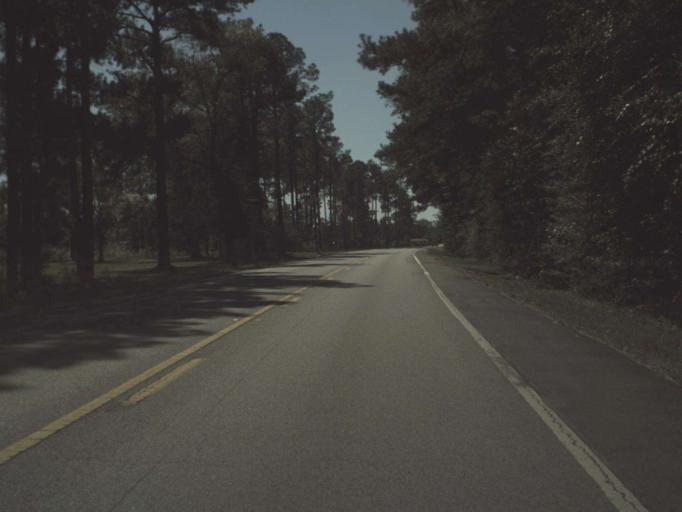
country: US
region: Florida
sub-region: Walton County
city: DeFuniak Springs
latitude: 30.8553
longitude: -86.1156
